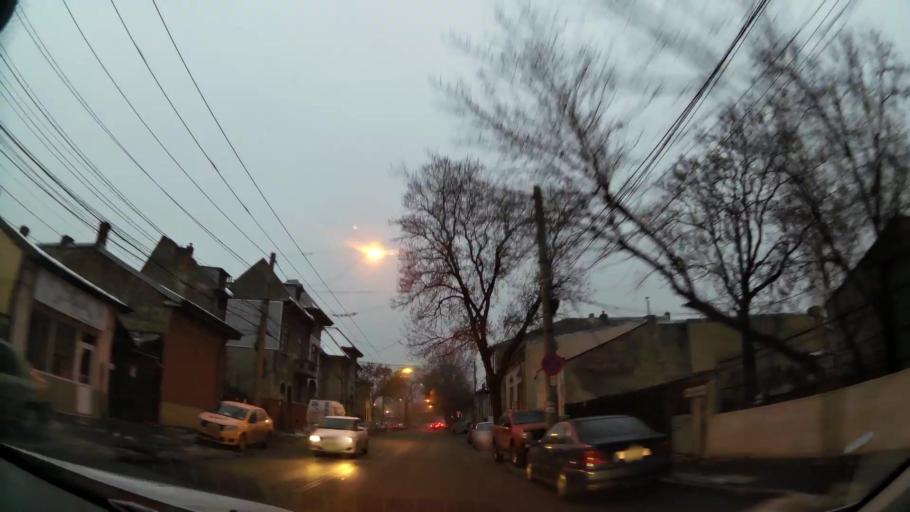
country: RO
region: Bucuresti
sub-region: Municipiul Bucuresti
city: Bucuresti
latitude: 44.4412
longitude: 26.0748
